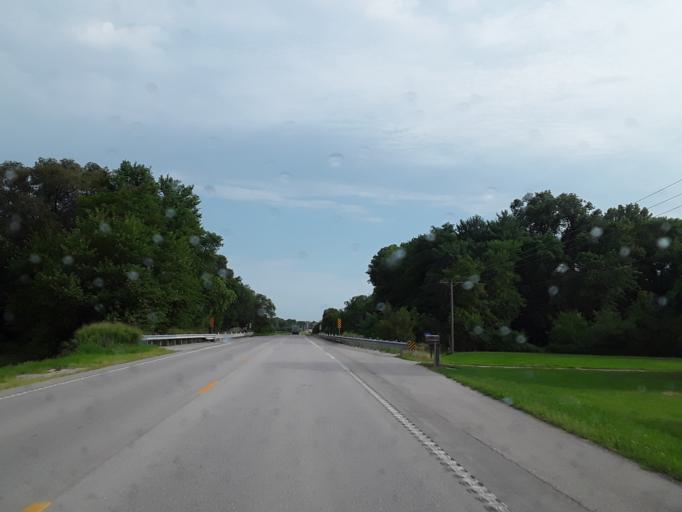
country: US
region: Nebraska
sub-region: Saunders County
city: Ashland
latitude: 41.0547
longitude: -96.3680
